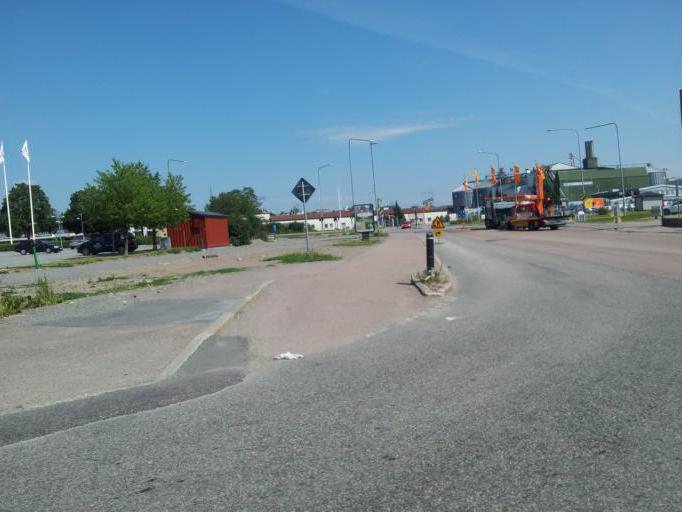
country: SE
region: Uppsala
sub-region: Uppsala Kommun
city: Uppsala
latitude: 59.8488
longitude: 17.6591
